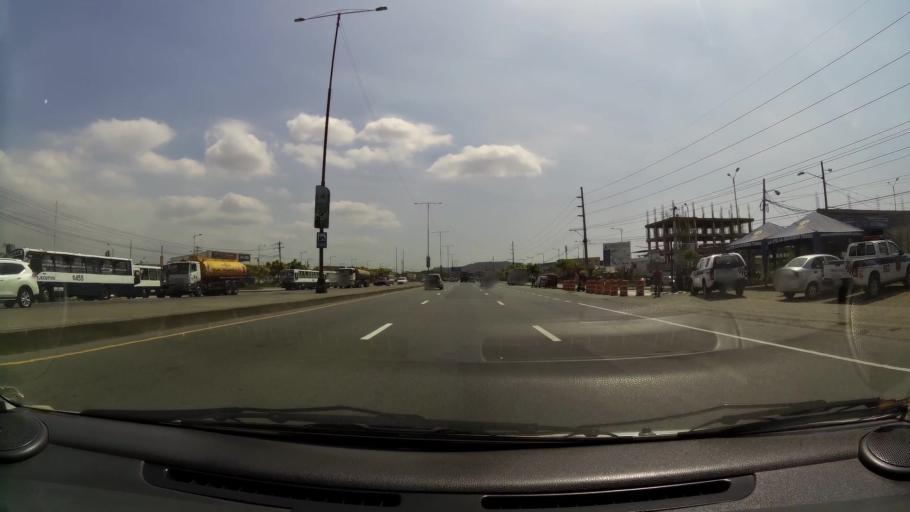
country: EC
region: Guayas
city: Eloy Alfaro
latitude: -2.0541
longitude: -79.8786
